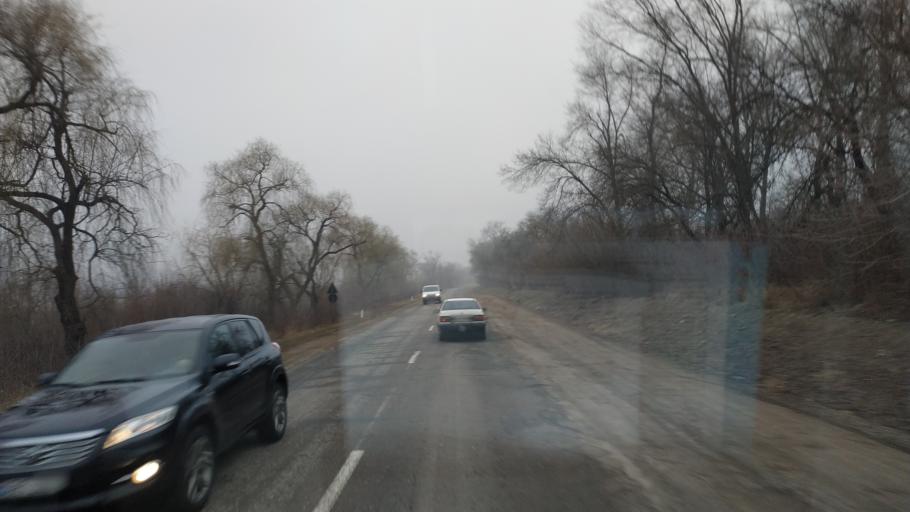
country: MD
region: Laloveni
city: Ialoveni
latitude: 46.9529
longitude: 28.7611
